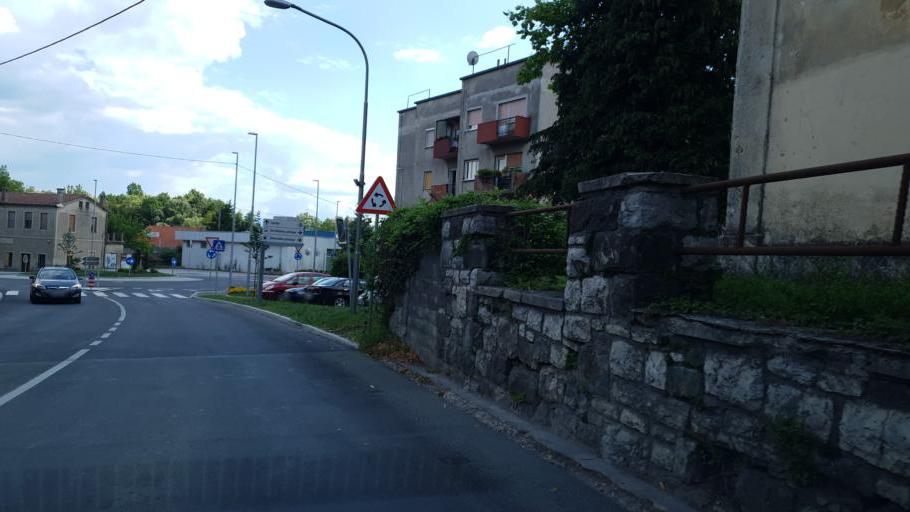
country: SI
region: Ilirska Bistrica
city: Ilirska Bistrica
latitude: 45.5670
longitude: 14.2428
